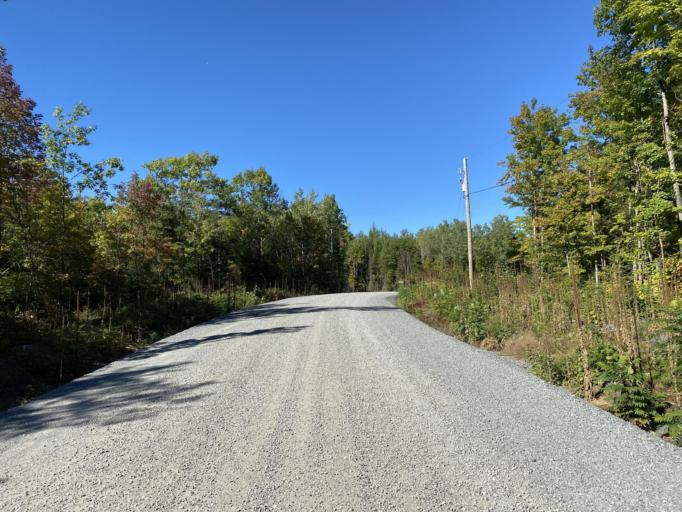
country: CA
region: Quebec
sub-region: Outaouais
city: Val-des-Monts
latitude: 45.5716
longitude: -75.5272
